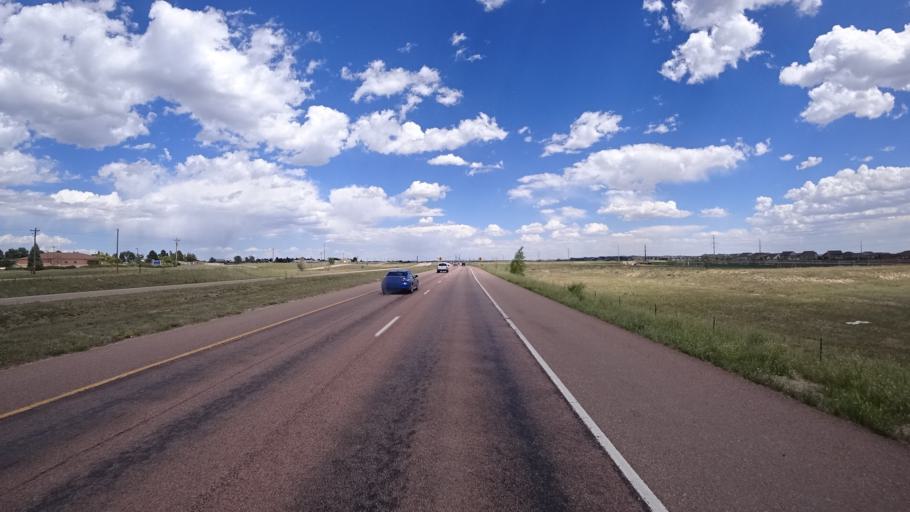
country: US
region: Colorado
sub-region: El Paso County
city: Black Forest
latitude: 38.9405
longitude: -104.6696
